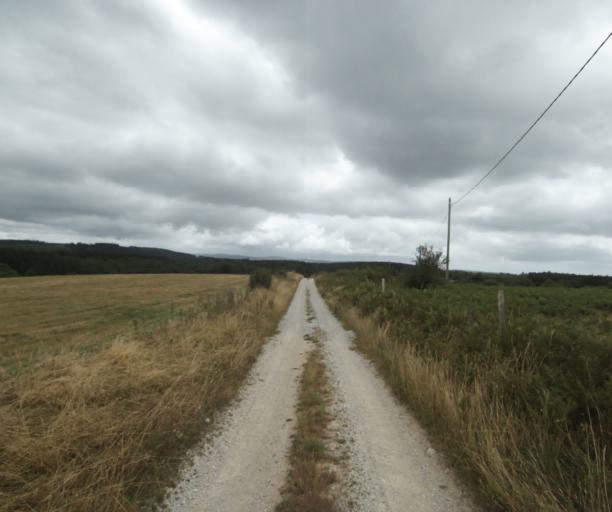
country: FR
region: Midi-Pyrenees
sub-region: Departement du Tarn
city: Soreze
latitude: 43.4323
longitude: 2.1066
